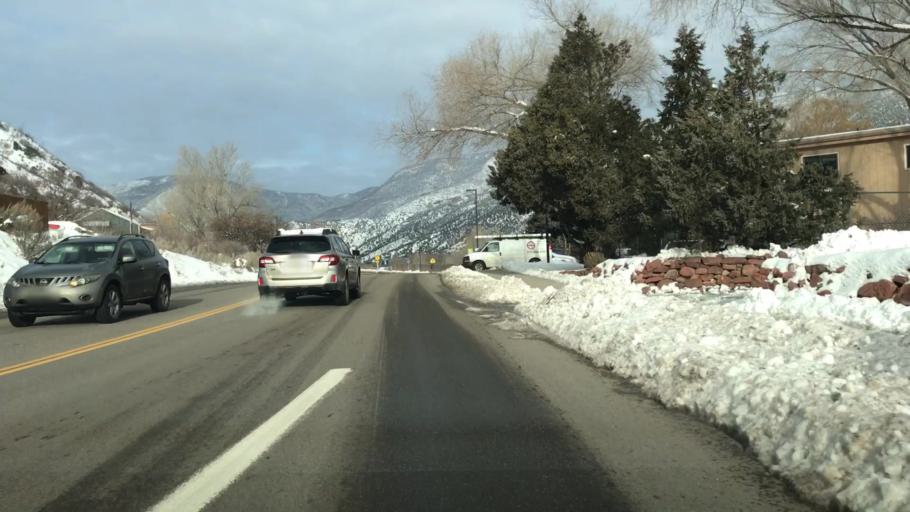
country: US
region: Colorado
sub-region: Garfield County
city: Glenwood Springs
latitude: 39.5473
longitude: -107.3323
